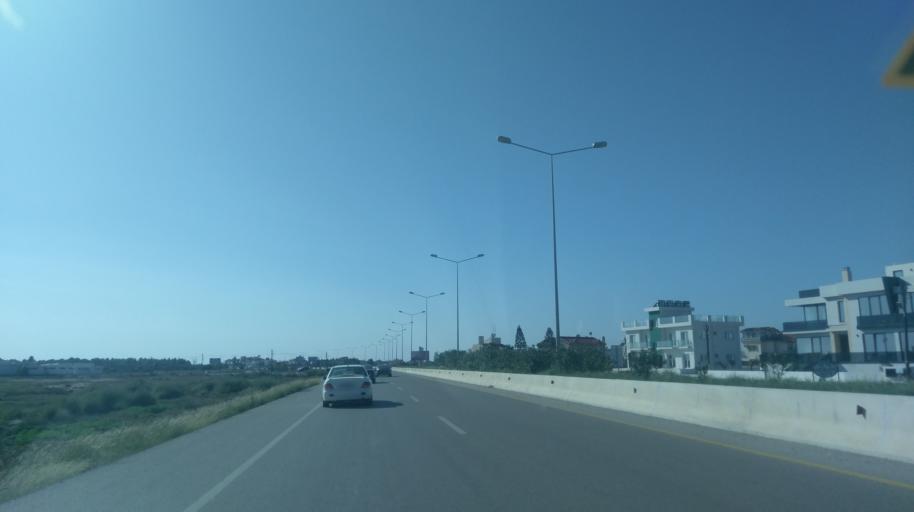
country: CY
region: Ammochostos
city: Trikomo
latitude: 35.2519
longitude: 33.9033
